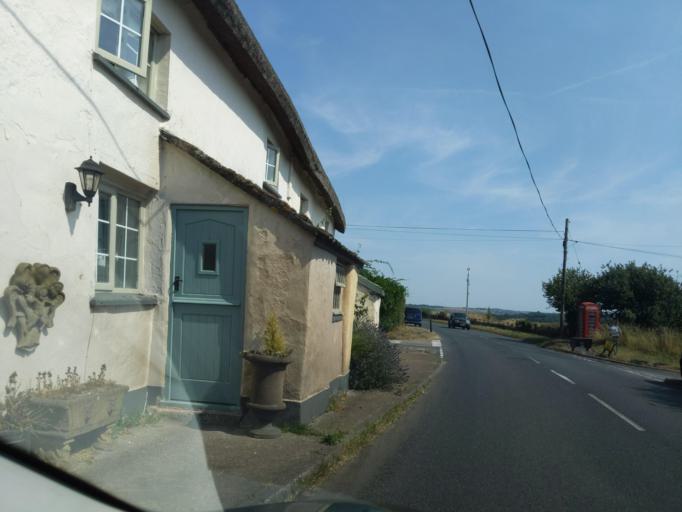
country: GB
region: England
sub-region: Devon
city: Winkleigh
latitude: 50.7930
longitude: -3.9517
